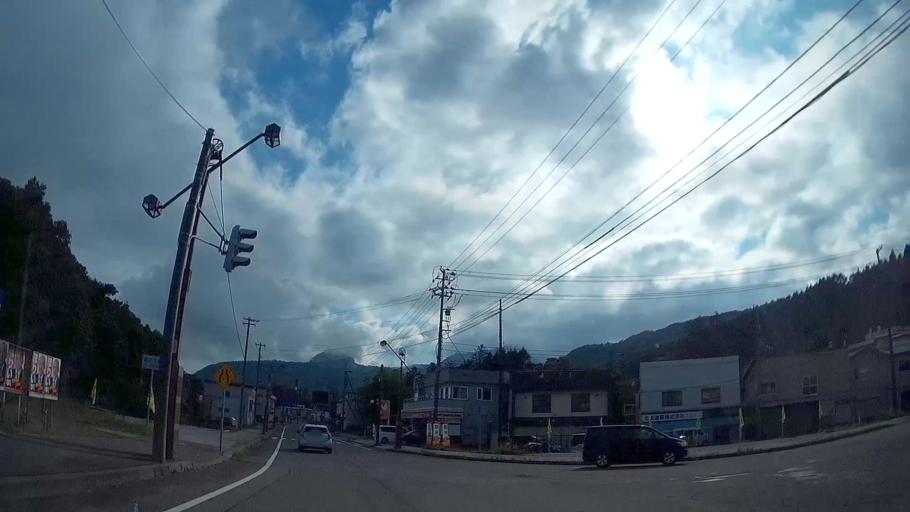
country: JP
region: Hokkaido
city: Date
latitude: 42.5573
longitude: 140.8877
